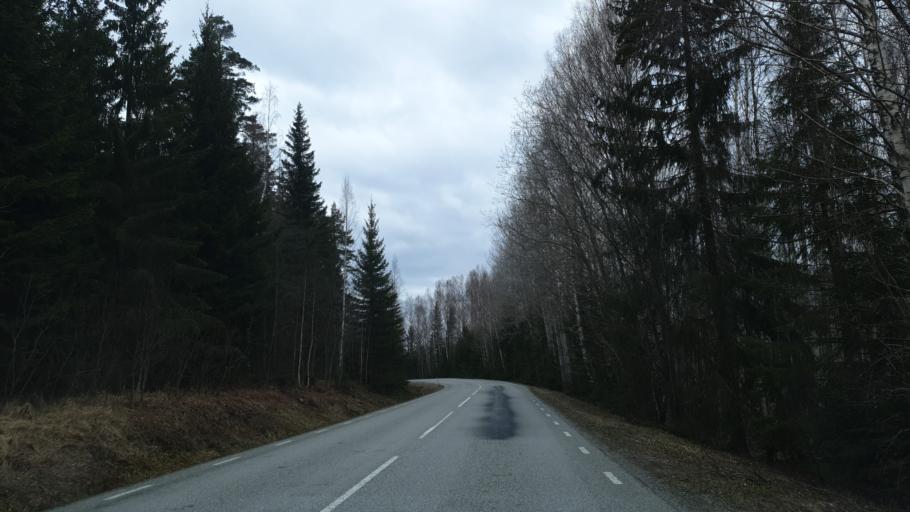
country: SE
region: OErebro
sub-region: Nora Kommun
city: As
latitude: 59.5797
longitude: 14.9802
